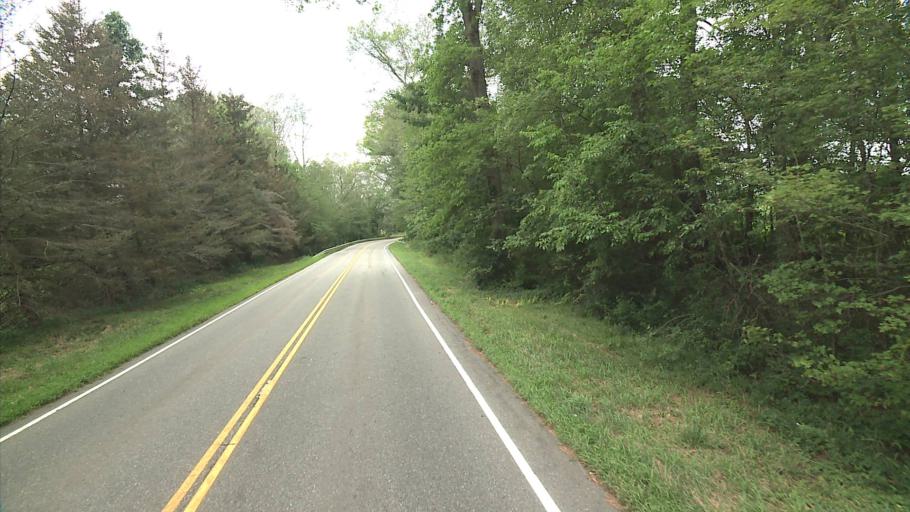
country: US
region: Connecticut
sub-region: Windham County
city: Wauregan
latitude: 41.7649
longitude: -71.9360
